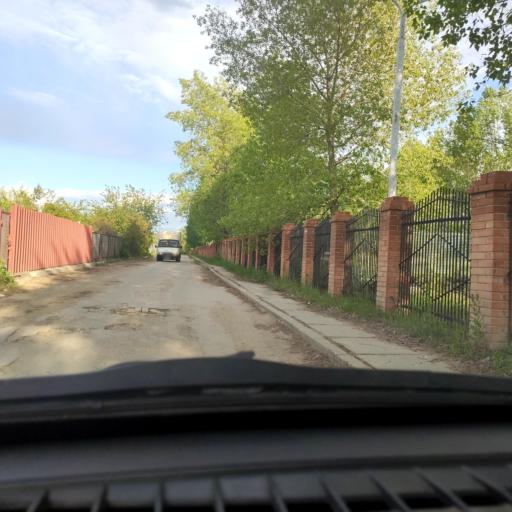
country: RU
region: Samara
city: Zhigulevsk
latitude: 53.4500
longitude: 49.5356
